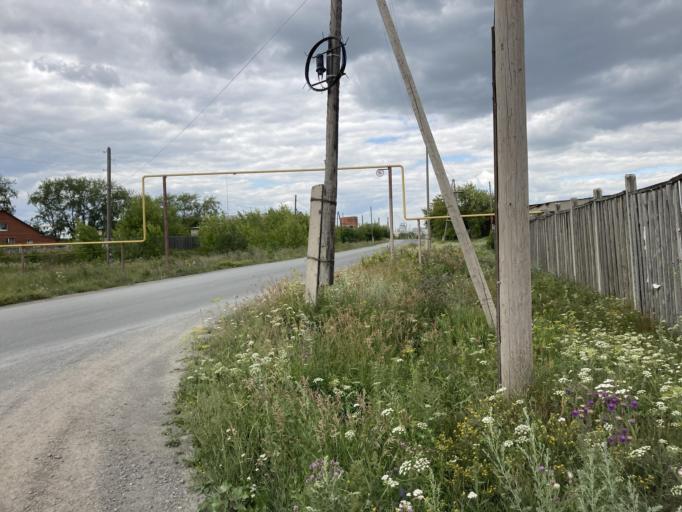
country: RU
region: Sverdlovsk
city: Bogdanovich
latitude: 56.7907
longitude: 62.0564
